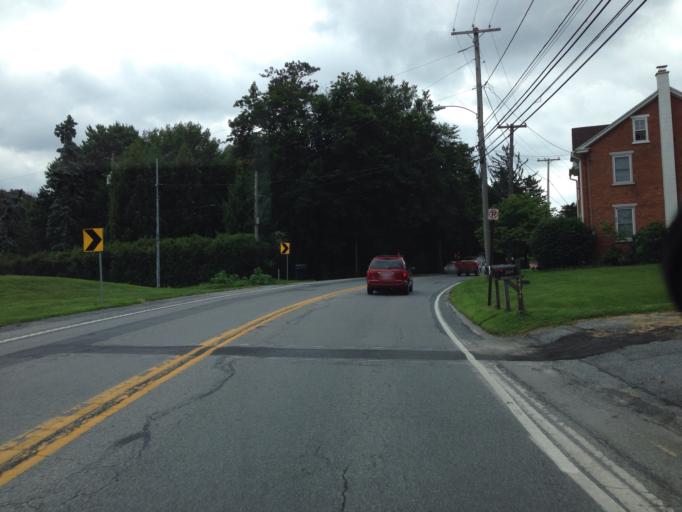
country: US
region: Pennsylvania
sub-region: Lancaster County
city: East Petersburg
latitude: 40.0931
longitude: -76.3038
